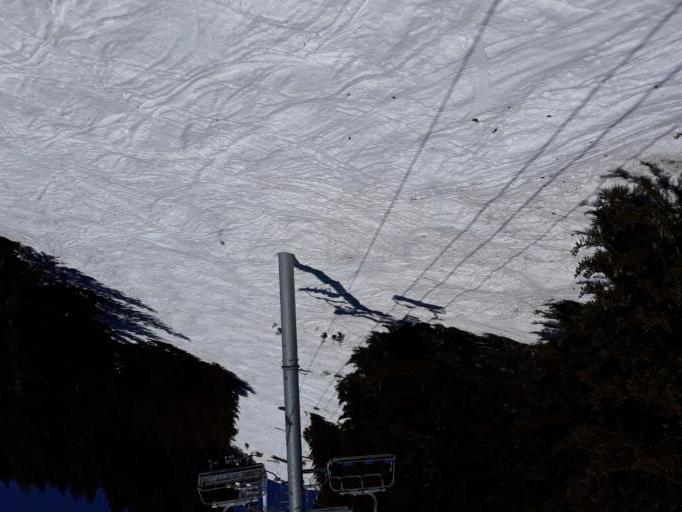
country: FR
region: Rhone-Alpes
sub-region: Departement de la Haute-Savoie
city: Araches-la-Frasse
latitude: 46.0319
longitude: 6.6757
